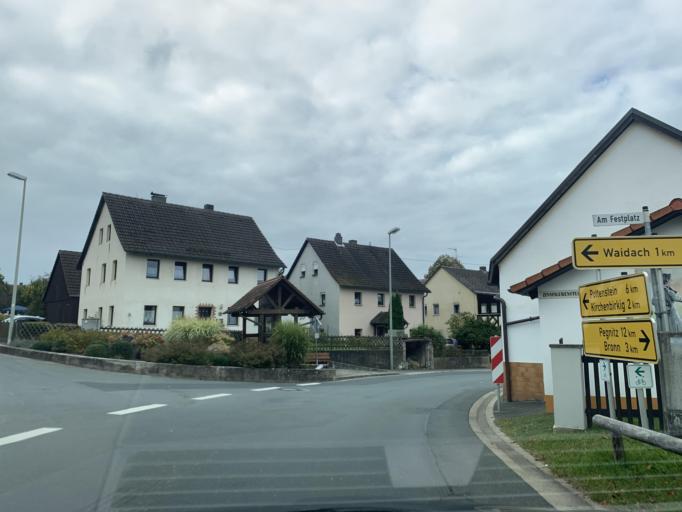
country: DE
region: Bavaria
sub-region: Upper Franconia
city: Pottenstein
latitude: 49.7365
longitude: 11.4204
